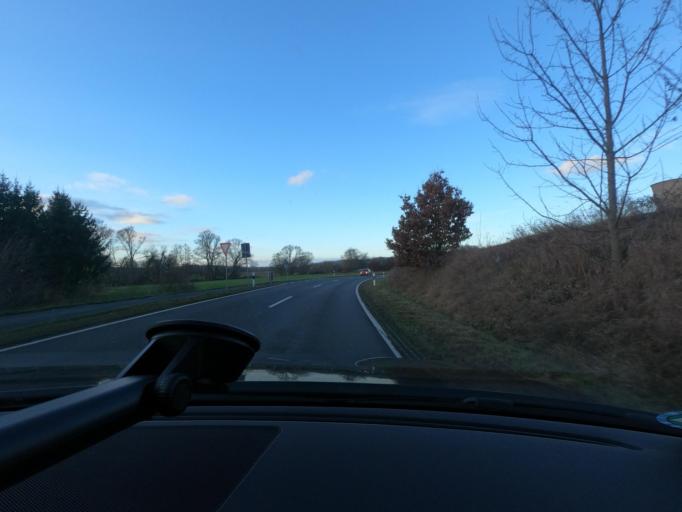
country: DE
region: Lower Saxony
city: Rhumspringe
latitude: 51.5732
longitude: 10.2988
